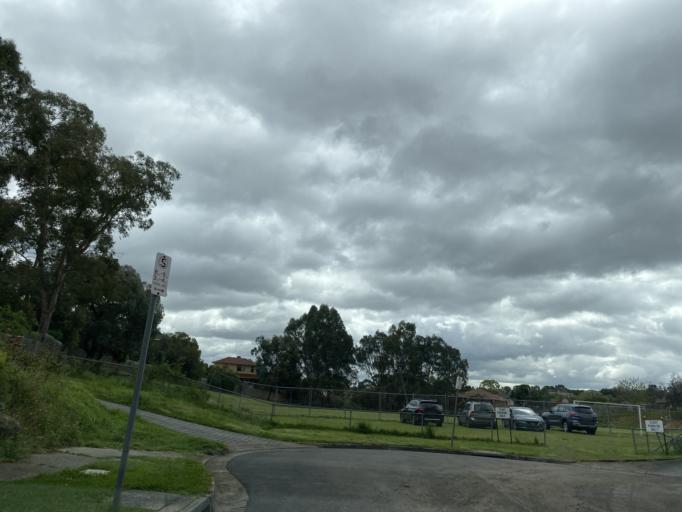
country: AU
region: Victoria
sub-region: Banyule
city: Darch
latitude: -37.7561
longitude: 145.1402
